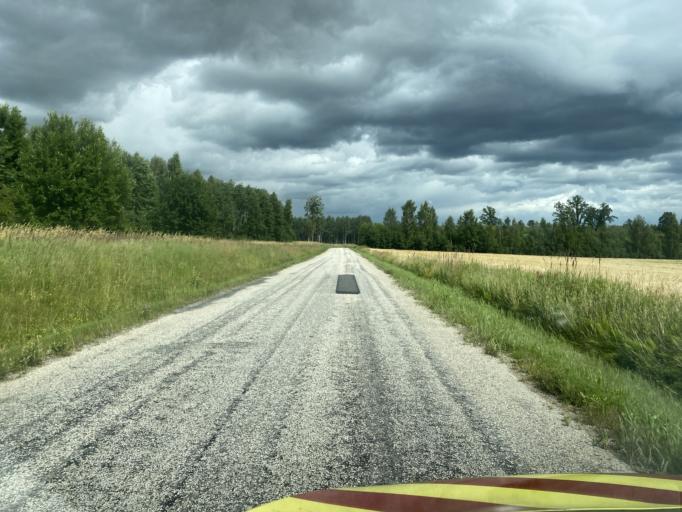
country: EE
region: Valgamaa
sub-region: Torva linn
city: Torva
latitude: 57.9575
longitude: 25.8867
